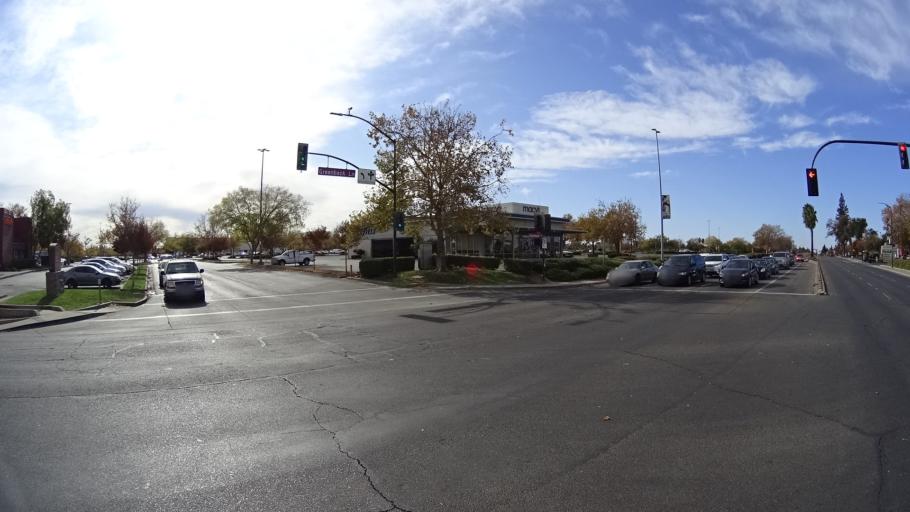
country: US
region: California
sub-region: Sacramento County
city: Citrus Heights
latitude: 38.6783
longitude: -121.2672
